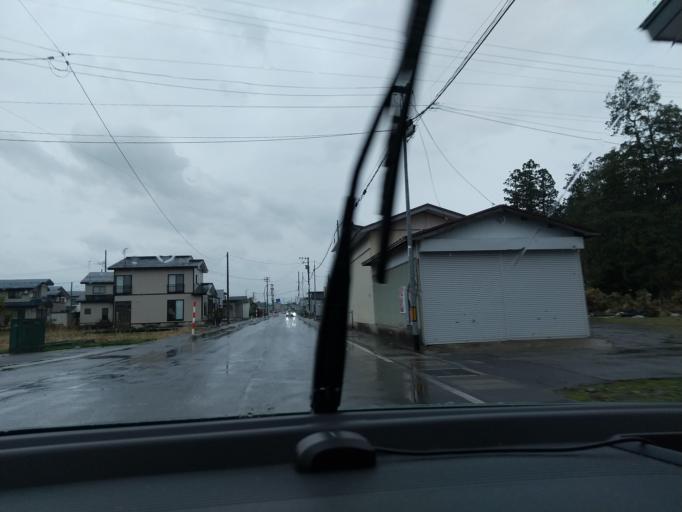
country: JP
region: Akita
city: Yokotemachi
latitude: 39.3044
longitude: 140.5416
